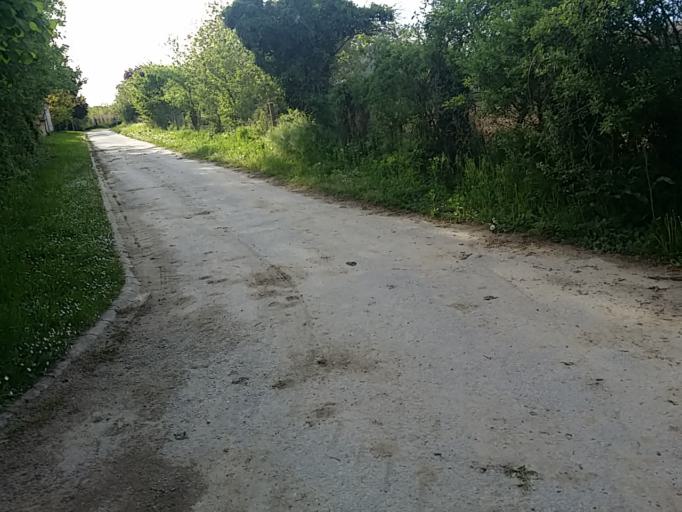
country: HR
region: Koprivnicko-Krizevacka
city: Ferdinandovac
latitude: 46.0905
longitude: 17.2366
